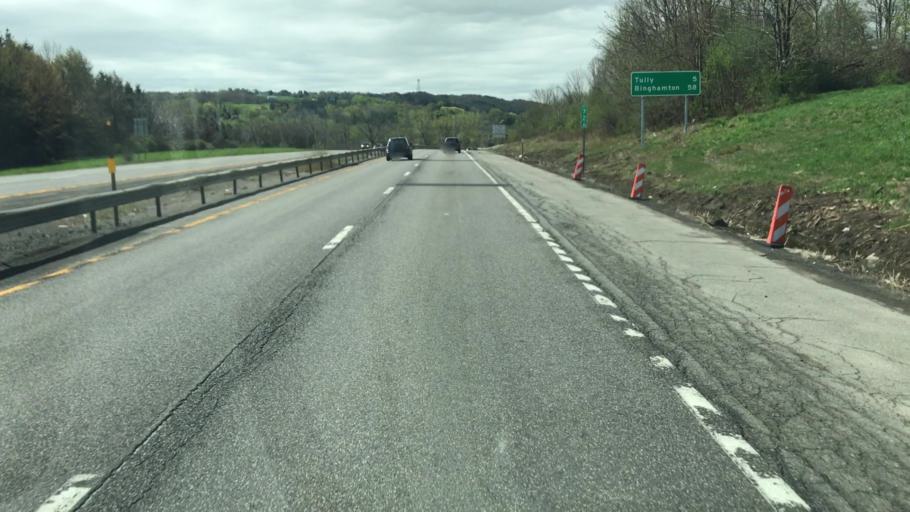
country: US
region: New York
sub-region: Onondaga County
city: Nedrow
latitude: 42.8760
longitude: -76.1105
